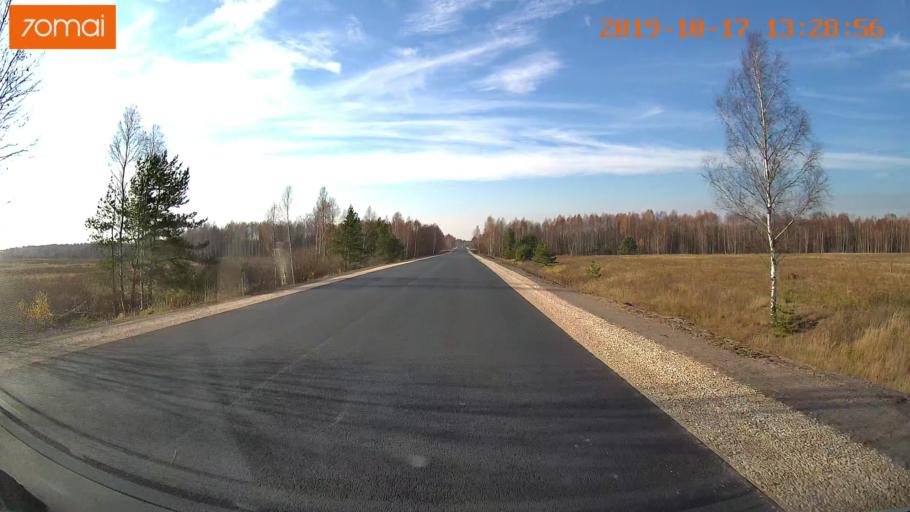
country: RU
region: Vladimir
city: Velikodvorskiy
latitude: 55.1178
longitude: 40.8547
